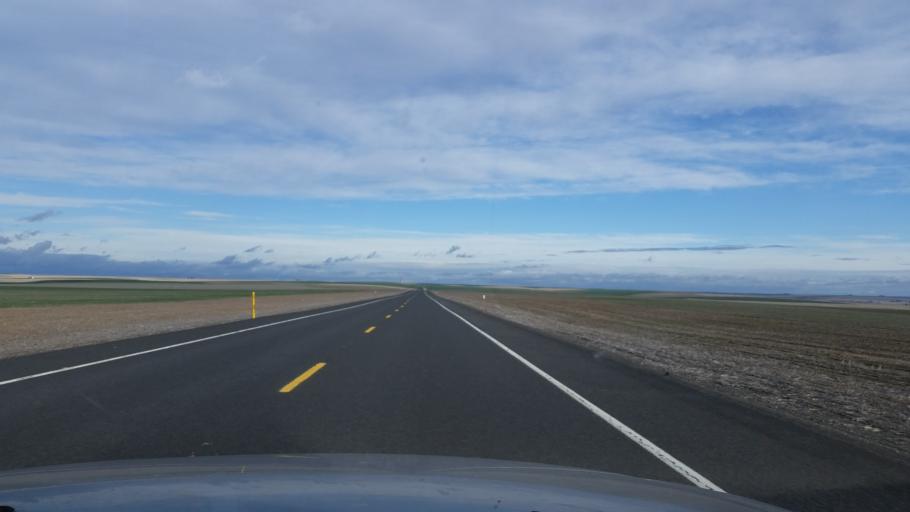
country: US
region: Washington
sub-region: Adams County
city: Ritzville
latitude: 47.3874
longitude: -118.4174
